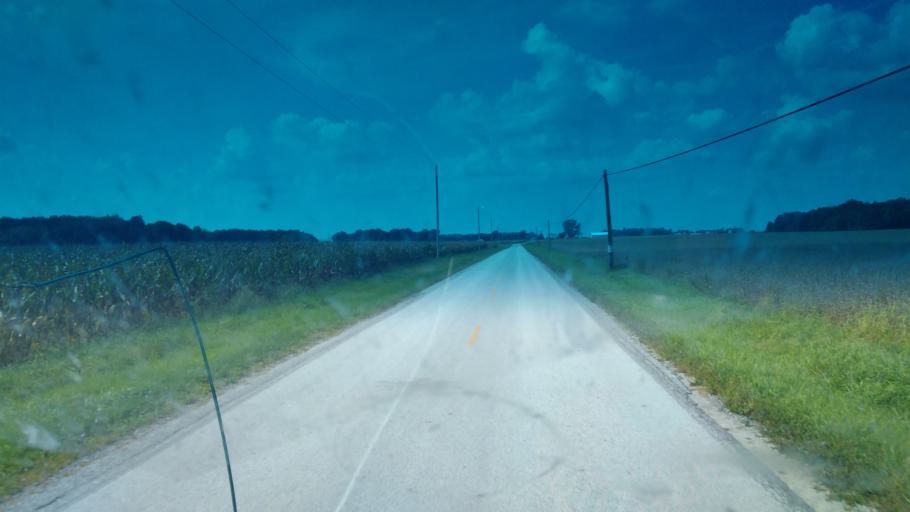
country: US
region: Ohio
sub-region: Hardin County
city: Kenton
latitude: 40.6431
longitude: -83.6618
